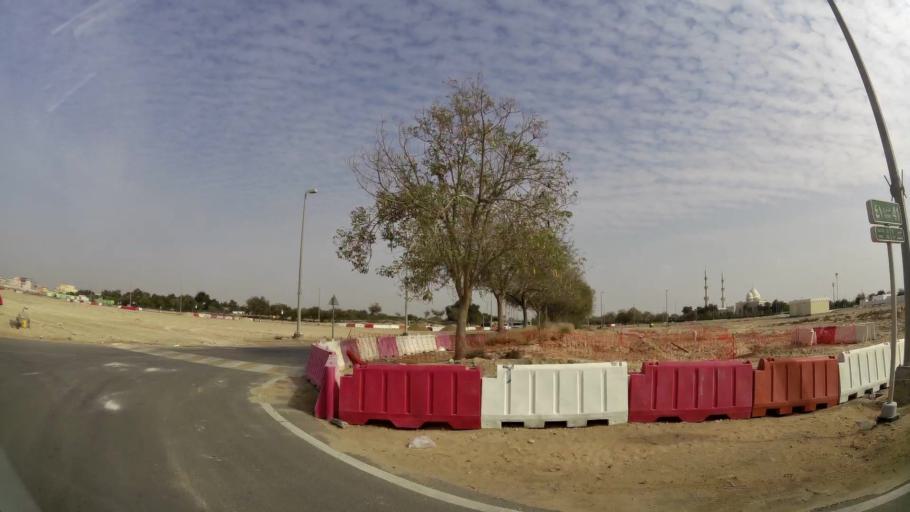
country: AE
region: Abu Dhabi
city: Abu Dhabi
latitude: 24.6149
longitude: 54.7054
